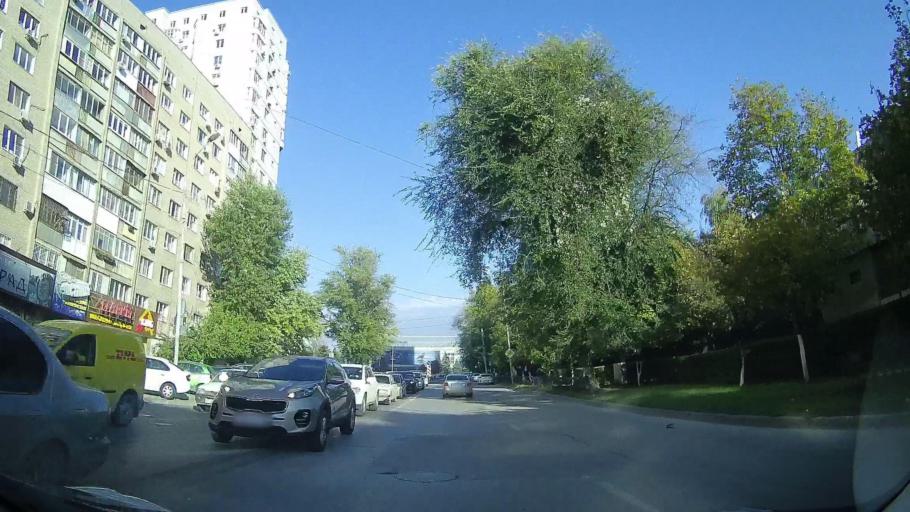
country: RU
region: Rostov
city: Rostov-na-Donu
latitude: 47.2353
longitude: 39.7164
